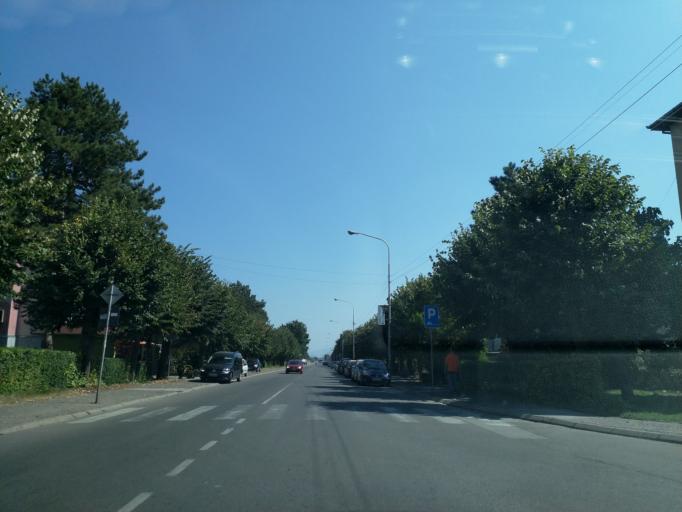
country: RS
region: Central Serbia
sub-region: Rasinski Okrug
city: Trstenik
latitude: 43.6177
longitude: 21.0069
